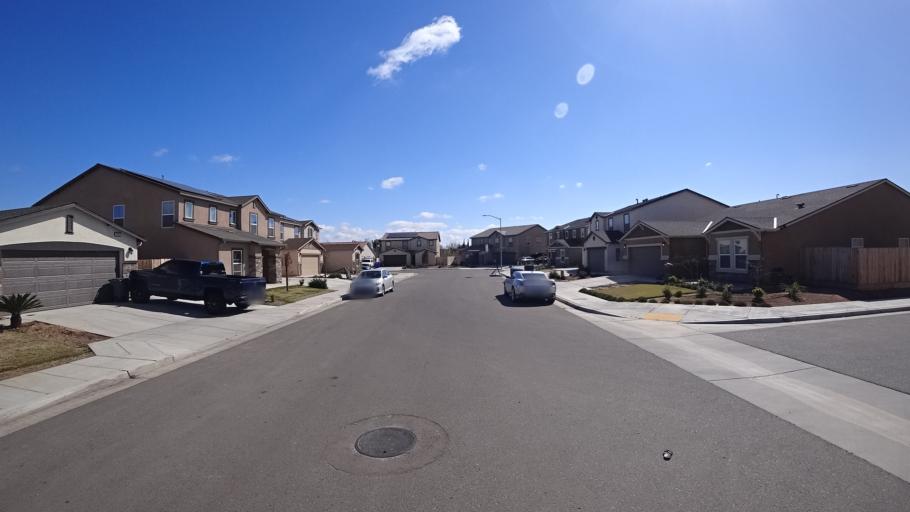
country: US
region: California
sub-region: Fresno County
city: West Park
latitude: 36.7888
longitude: -119.8908
